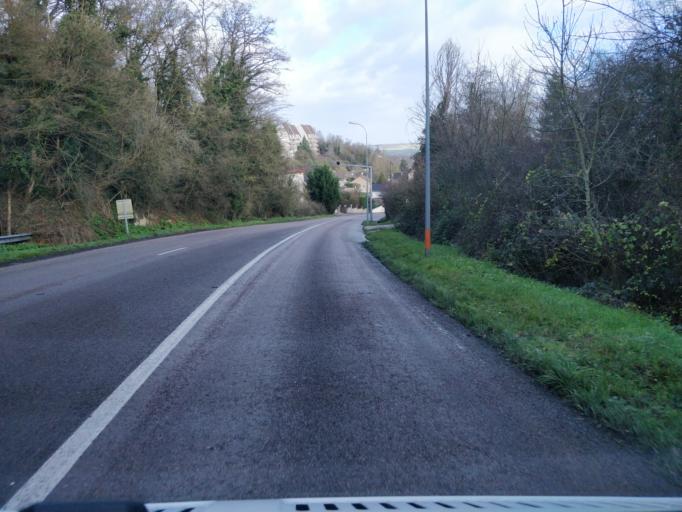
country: FR
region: Bourgogne
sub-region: Departement de l'Yonne
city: Paron
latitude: 48.1937
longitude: 3.2565
